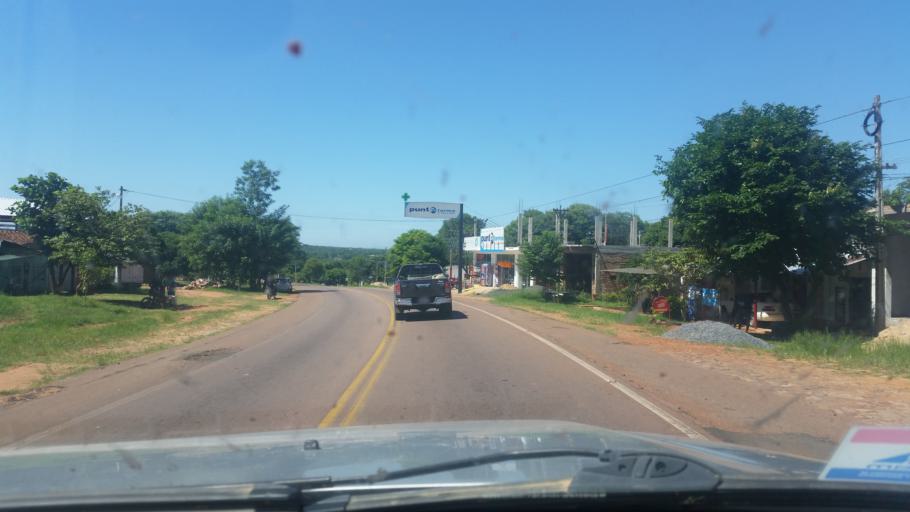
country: PY
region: Paraguari
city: Quiindy
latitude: -25.8823
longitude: -57.2898
